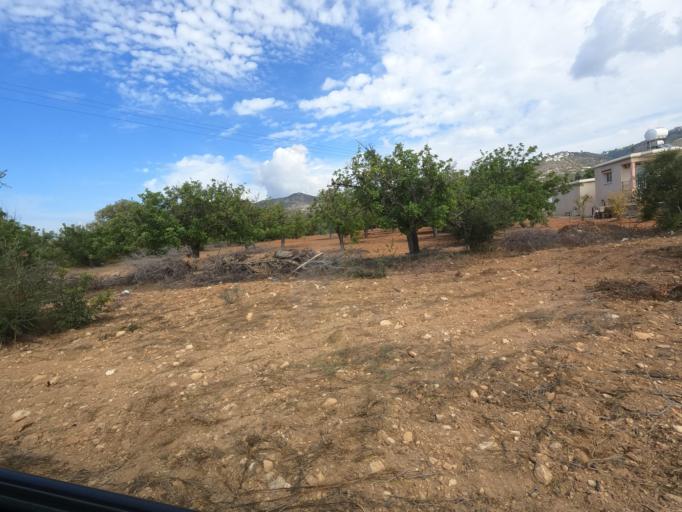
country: CY
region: Pafos
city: Mesogi
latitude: 34.8197
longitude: 32.4560
